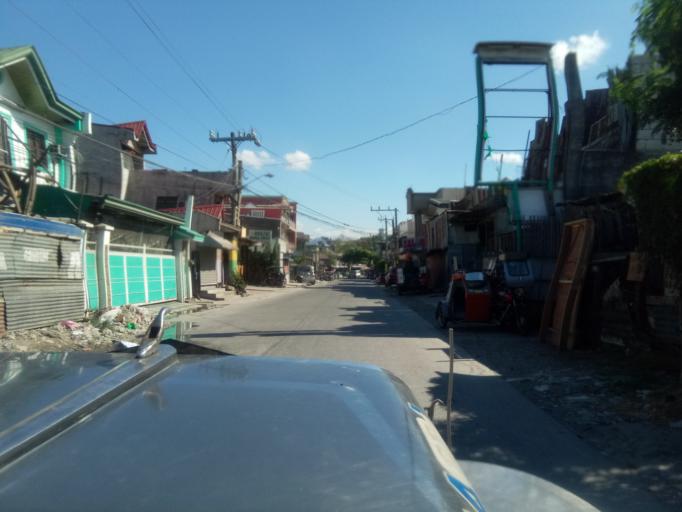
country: PH
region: Calabarzon
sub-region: Province of Cavite
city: Dasmarinas
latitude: 14.3119
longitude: 120.9706
